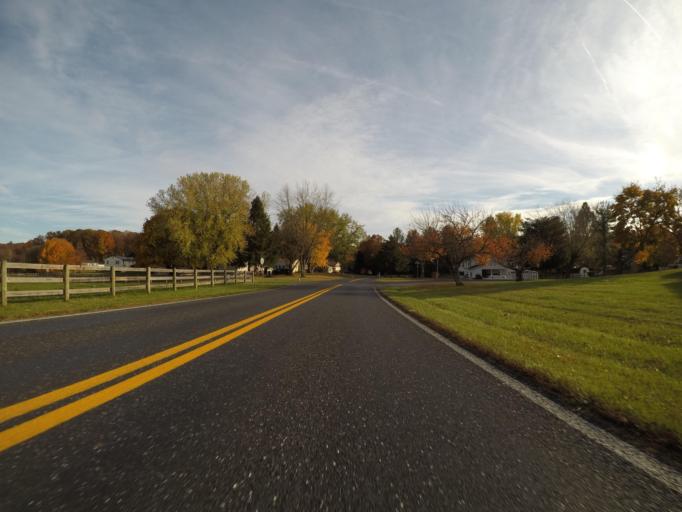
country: US
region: Maryland
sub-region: Carroll County
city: Hampstead
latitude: 39.5801
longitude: -76.8979
